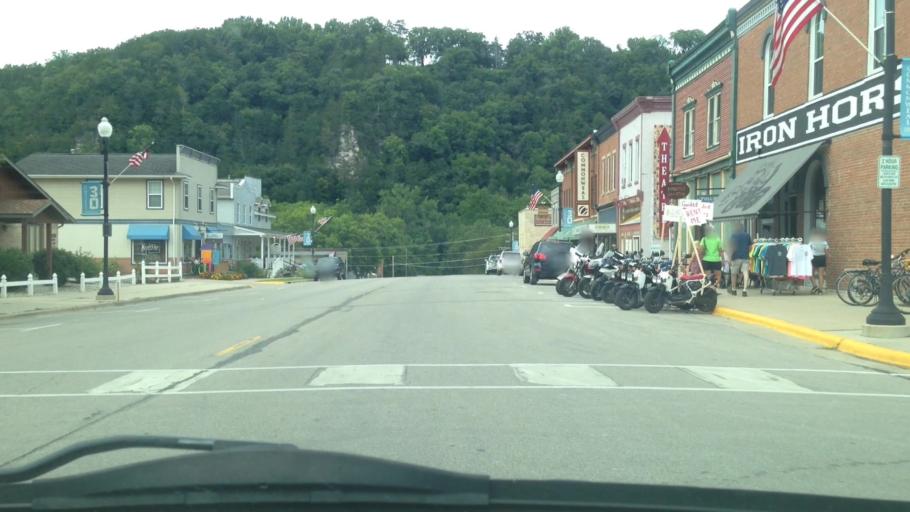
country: US
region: Minnesota
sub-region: Fillmore County
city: Preston
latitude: 43.7220
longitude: -91.9770
